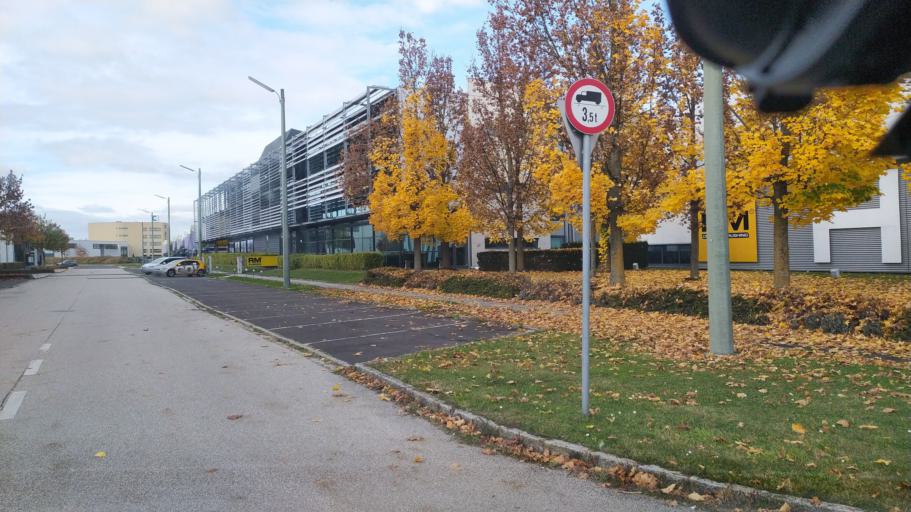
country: AT
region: Upper Austria
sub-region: Politischer Bezirk Urfahr-Umgebung
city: Steyregg
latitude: 48.2534
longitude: 14.3797
